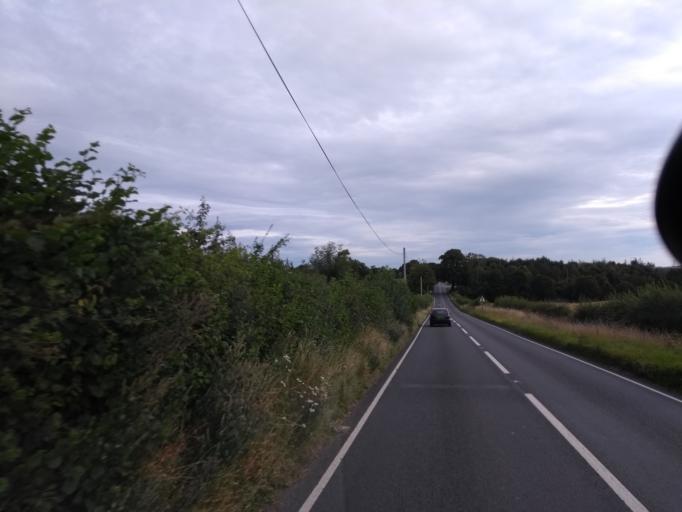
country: GB
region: England
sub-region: Somerset
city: Crewkerne
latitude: 50.8584
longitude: -2.7717
